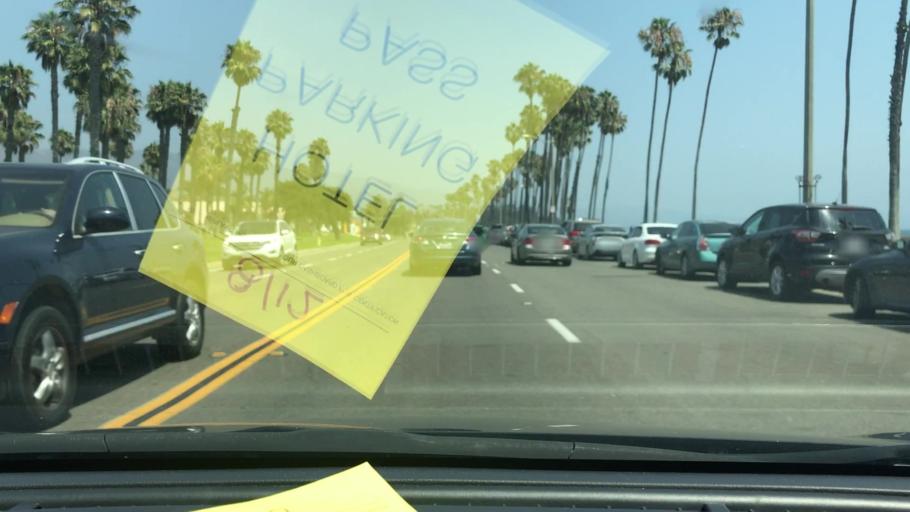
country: US
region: California
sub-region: Santa Barbara County
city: Santa Barbara
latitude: 34.4156
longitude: -119.6780
